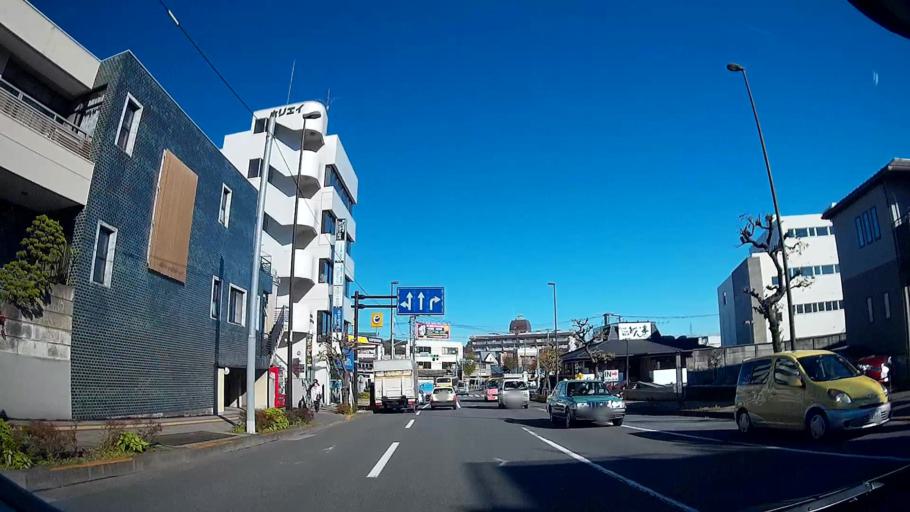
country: JP
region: Tokyo
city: Hachioji
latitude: 35.6629
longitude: 139.3396
